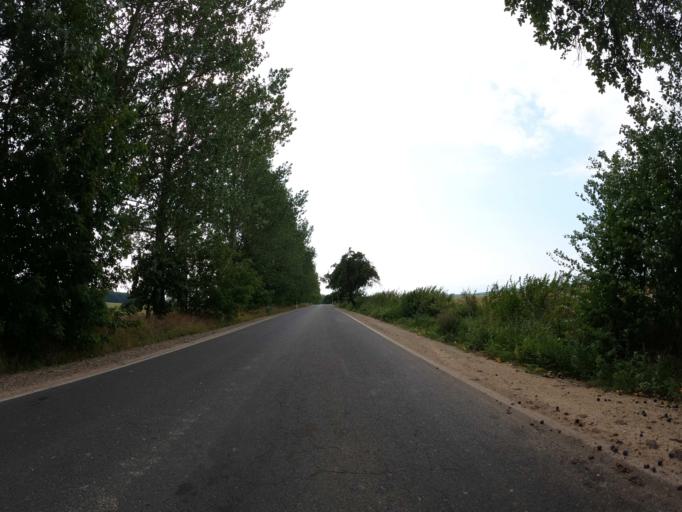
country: DE
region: Mecklenburg-Vorpommern
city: Malchow
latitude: 53.4490
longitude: 12.5120
